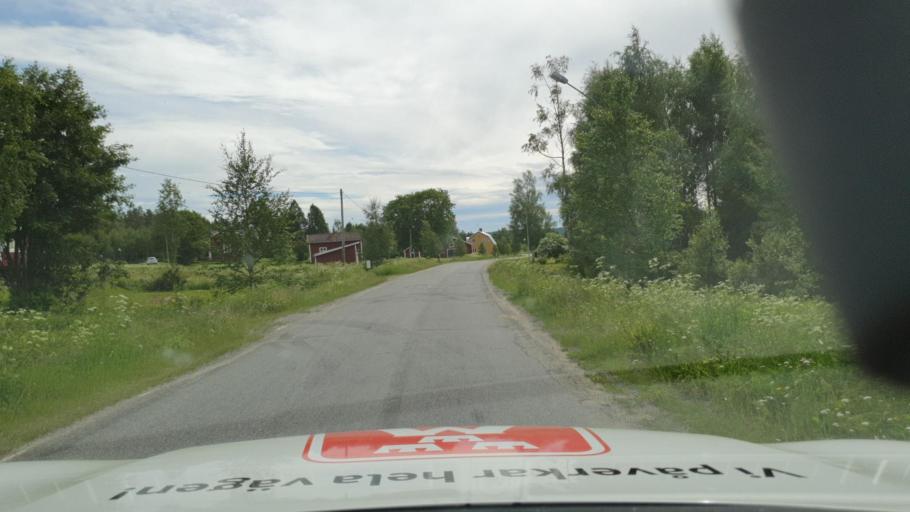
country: SE
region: Vaesterbotten
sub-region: Skelleftea Kommun
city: Burtraesk
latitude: 64.4910
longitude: 20.5054
